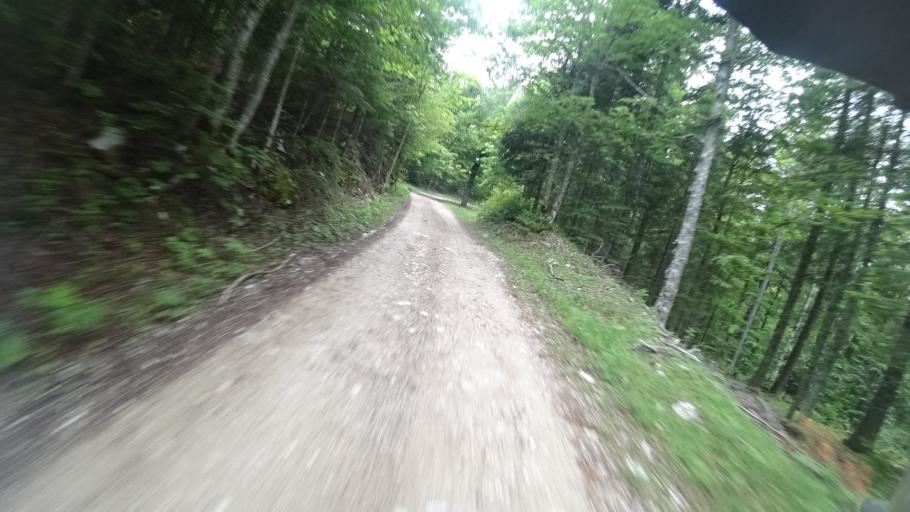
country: BA
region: Federation of Bosnia and Herzegovina
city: Bihac
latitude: 44.6315
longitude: 15.8379
